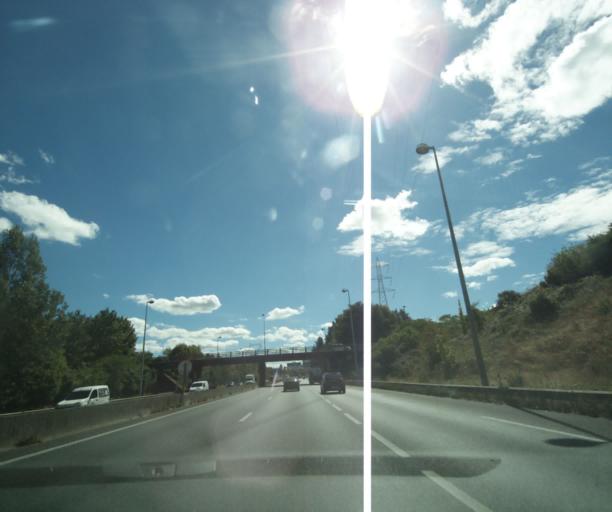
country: FR
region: Aquitaine
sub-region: Departement de la Gironde
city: Artigues-pres-Bordeaux
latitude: 44.8487
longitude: -0.5035
